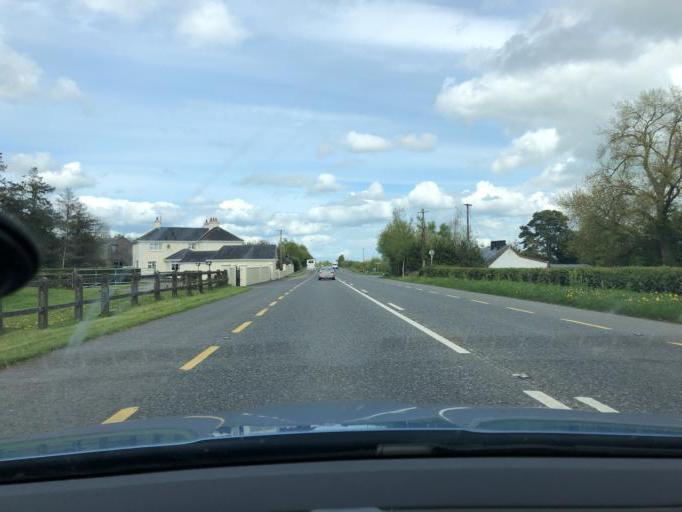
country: IE
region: Leinster
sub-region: Laois
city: Portlaoise
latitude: 52.9910
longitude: -7.3119
